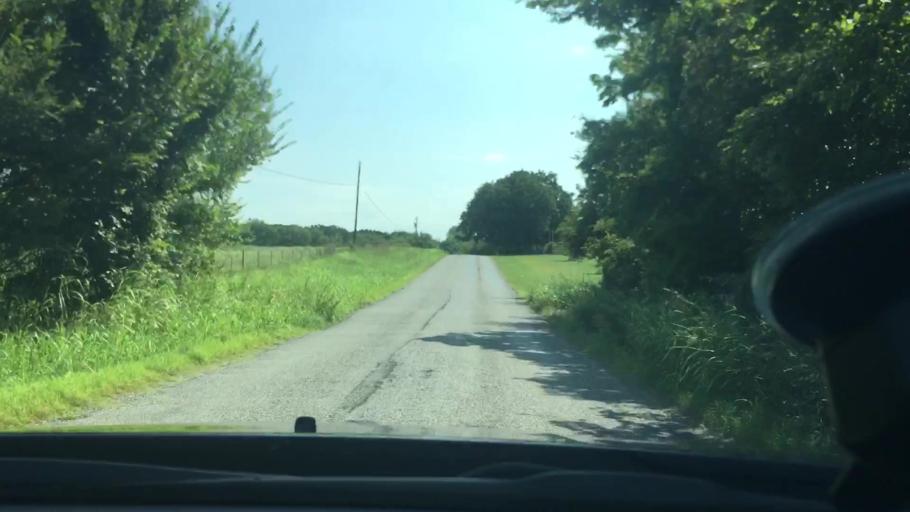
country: US
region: Oklahoma
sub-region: Bryan County
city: Colbert
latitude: 33.9110
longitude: -96.5223
